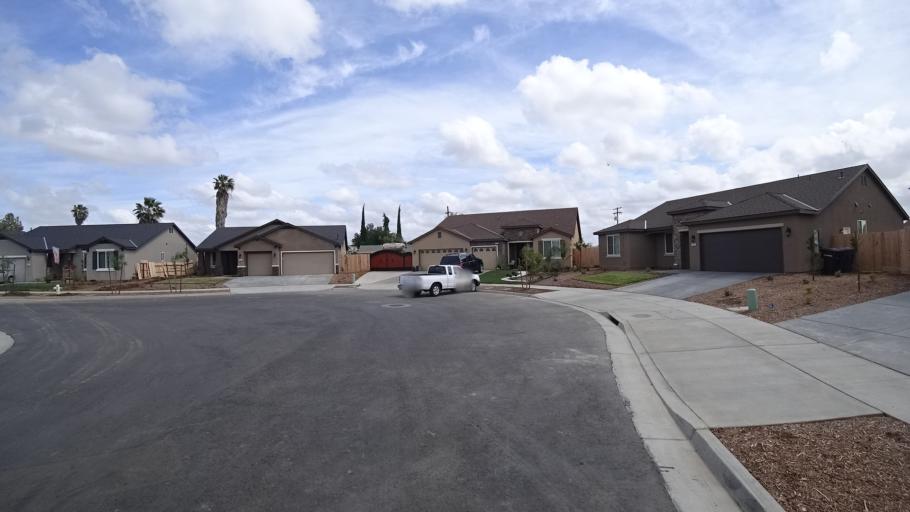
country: US
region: California
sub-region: Kings County
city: Hanford
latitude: 36.3090
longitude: -119.6704
